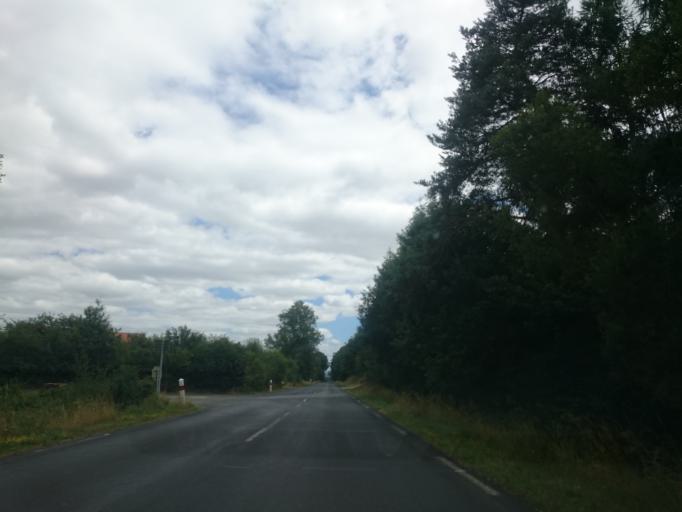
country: FR
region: Auvergne
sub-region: Departement du Cantal
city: Laroquebrou
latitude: 44.9666
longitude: 2.2443
